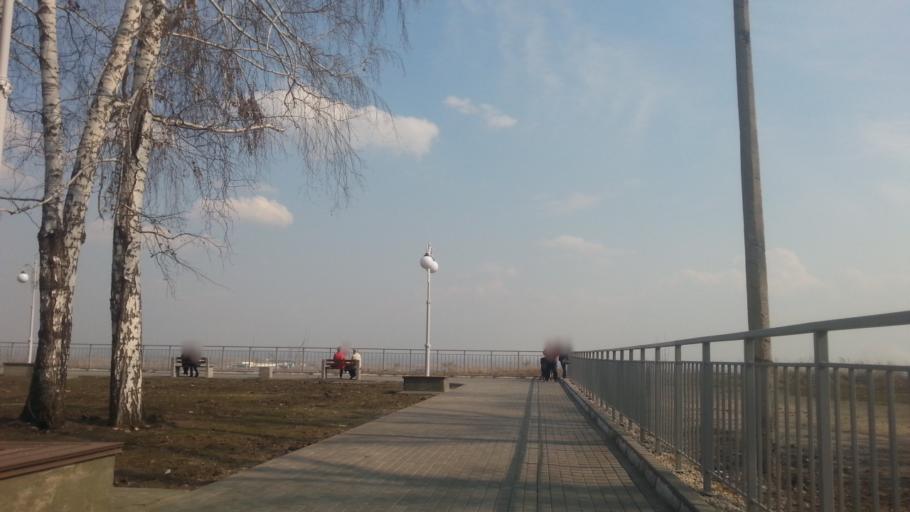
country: RU
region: Altai Krai
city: Zaton
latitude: 53.3212
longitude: 83.7935
